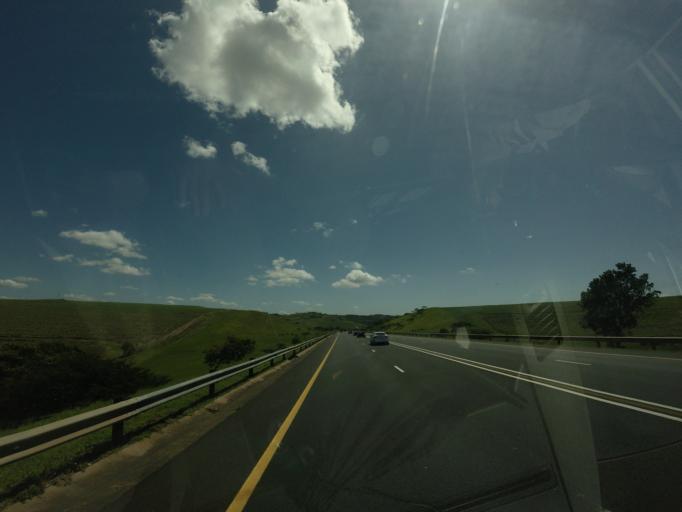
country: ZA
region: KwaZulu-Natal
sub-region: iLembe District Municipality
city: Mandeni
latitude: -29.1045
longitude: 31.5827
